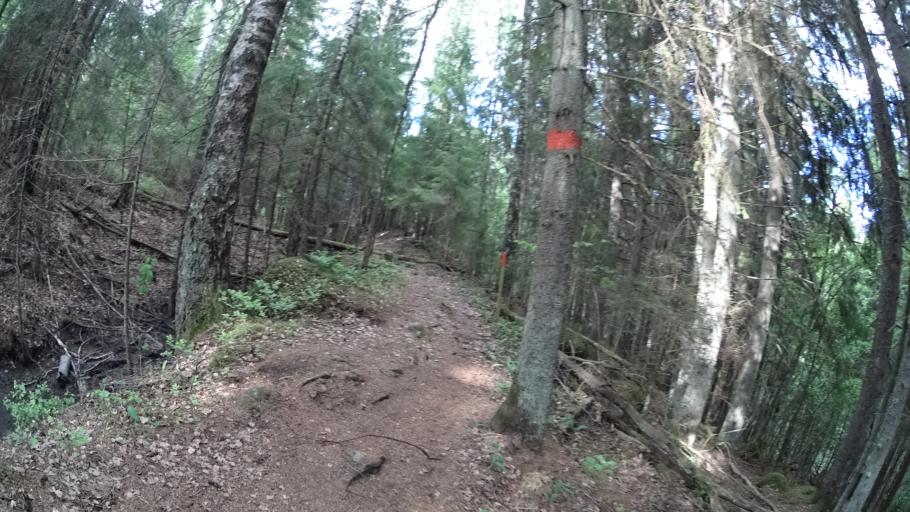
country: FI
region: Uusimaa
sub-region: Raaseporin
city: Pohja
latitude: 60.1451
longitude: 23.5401
